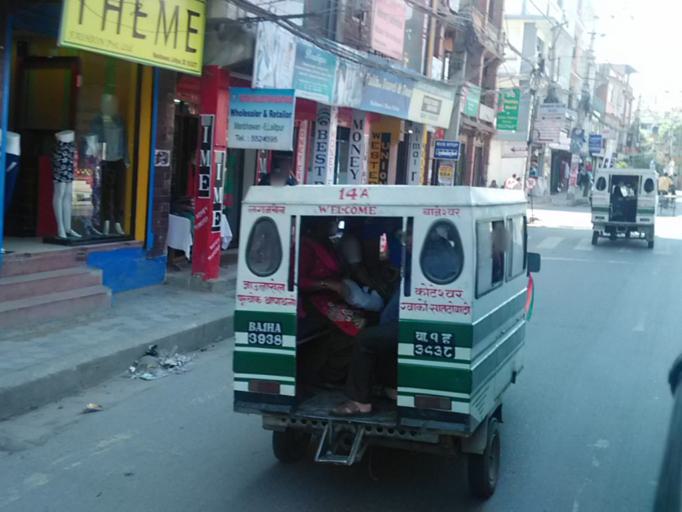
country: NP
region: Central Region
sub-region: Bagmati Zone
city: Patan
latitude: 27.6720
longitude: 85.3165
